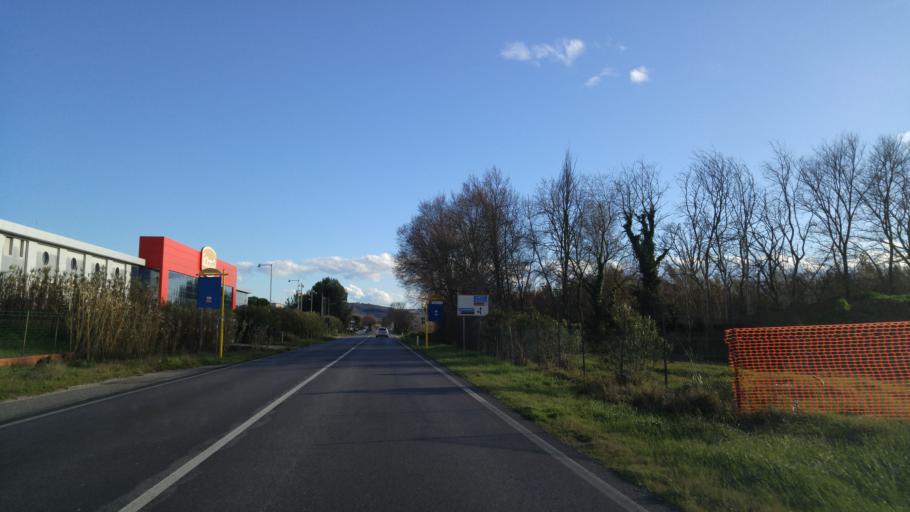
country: IT
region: The Marches
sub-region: Provincia di Ancona
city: Camerano
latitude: 43.5153
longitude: 13.5395
